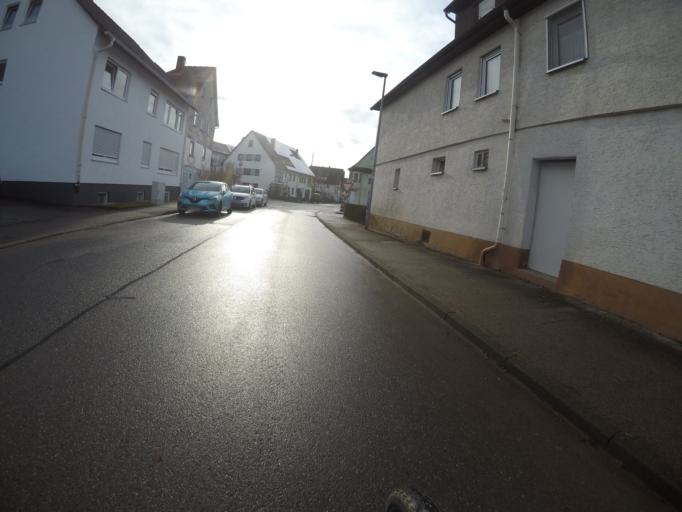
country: DE
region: Baden-Wuerttemberg
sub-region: Regierungsbezirk Stuttgart
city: Deckenpfronn
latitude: 48.6524
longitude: 8.8210
